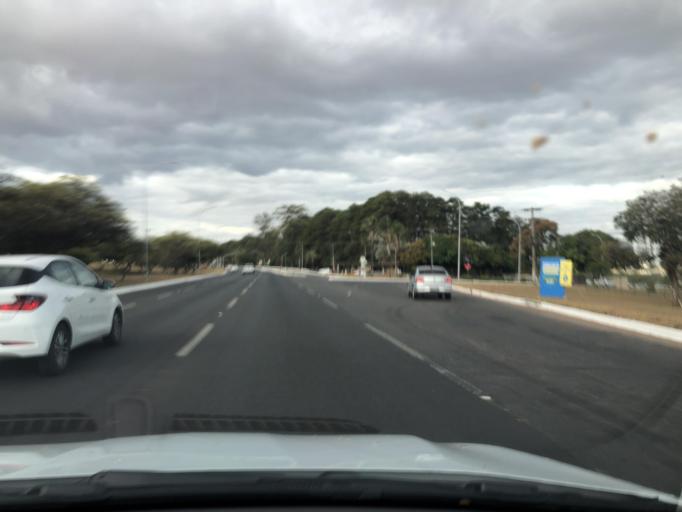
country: BR
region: Federal District
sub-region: Brasilia
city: Brasilia
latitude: -15.8076
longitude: -47.9297
